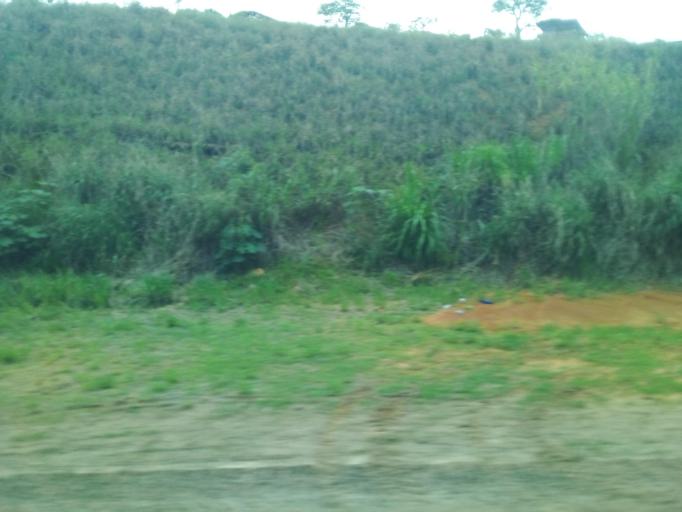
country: BR
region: Minas Gerais
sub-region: Nova Era
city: Nova Era
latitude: -19.7514
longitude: -43.0224
